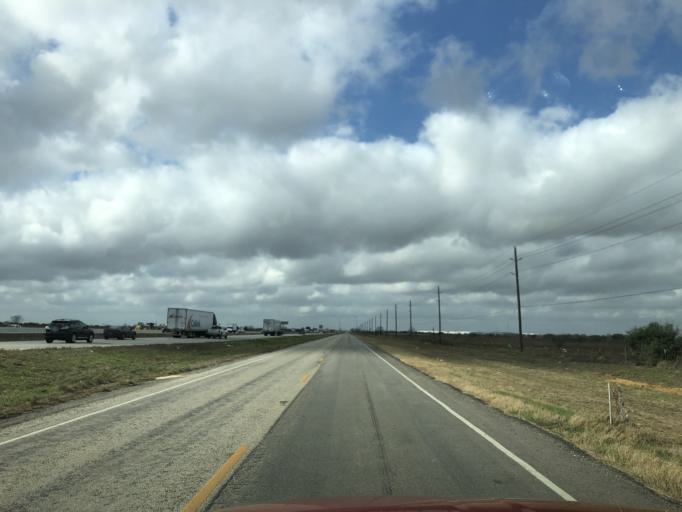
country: US
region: Texas
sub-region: Austin County
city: Sealy
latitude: 29.7640
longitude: -96.1915
